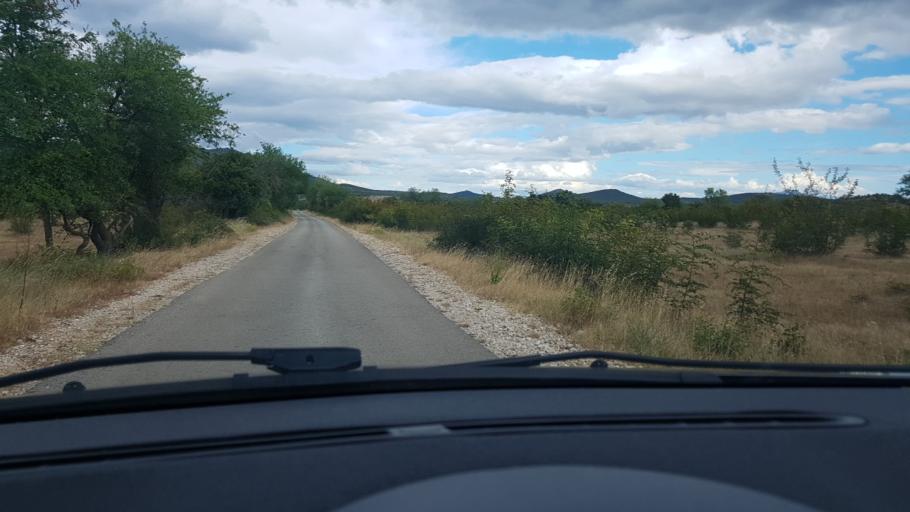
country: HR
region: Sibensko-Kniniska
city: Kistanje
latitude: 44.1079
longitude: 15.9316
